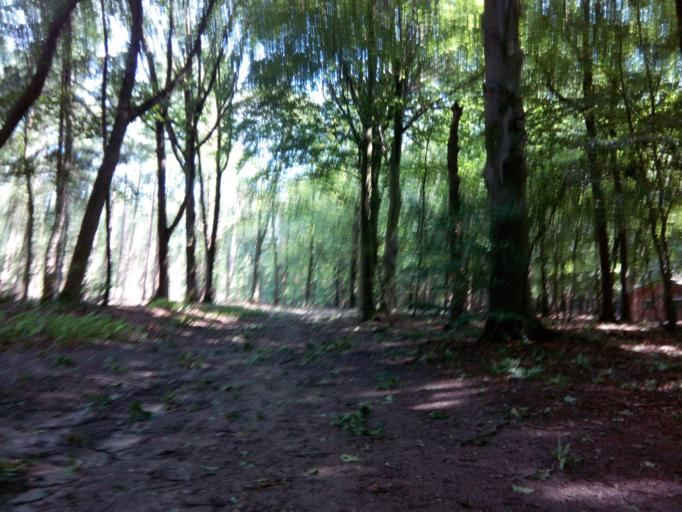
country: NL
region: Utrecht
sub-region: Gemeente Utrechtse Heuvelrug
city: Doorn
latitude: 52.0496
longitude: 5.3472
